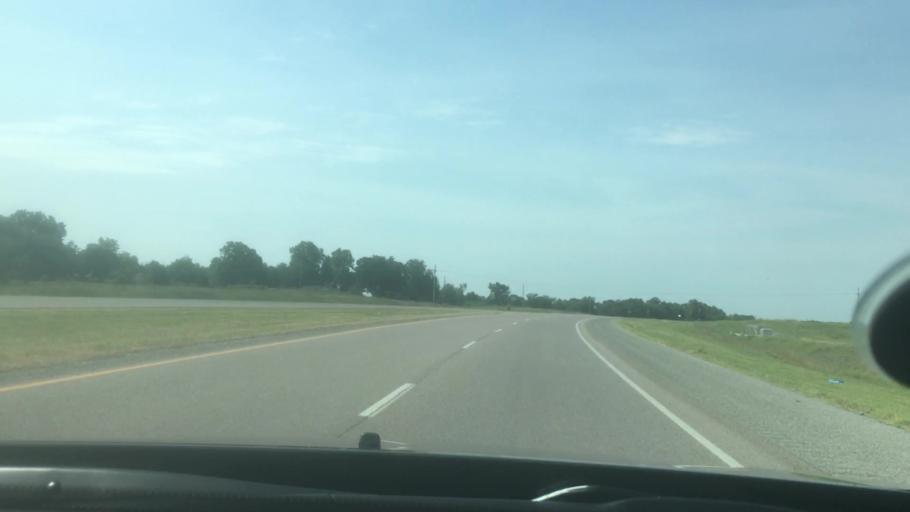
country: US
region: Oklahoma
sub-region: Pontotoc County
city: Ada
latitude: 34.8207
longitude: -96.6933
